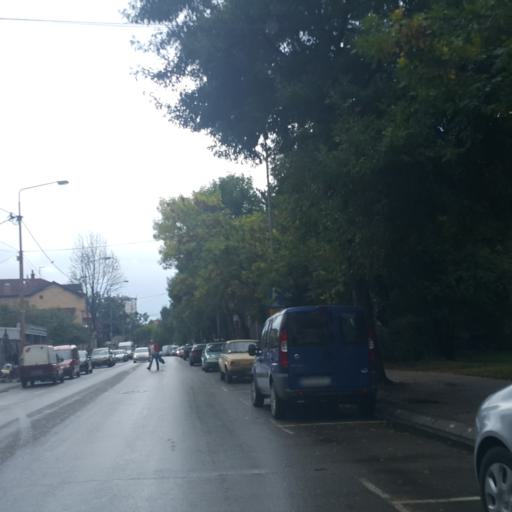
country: RS
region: Central Serbia
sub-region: Rasinski Okrug
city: Krusevac
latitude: 43.5747
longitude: 21.3379
